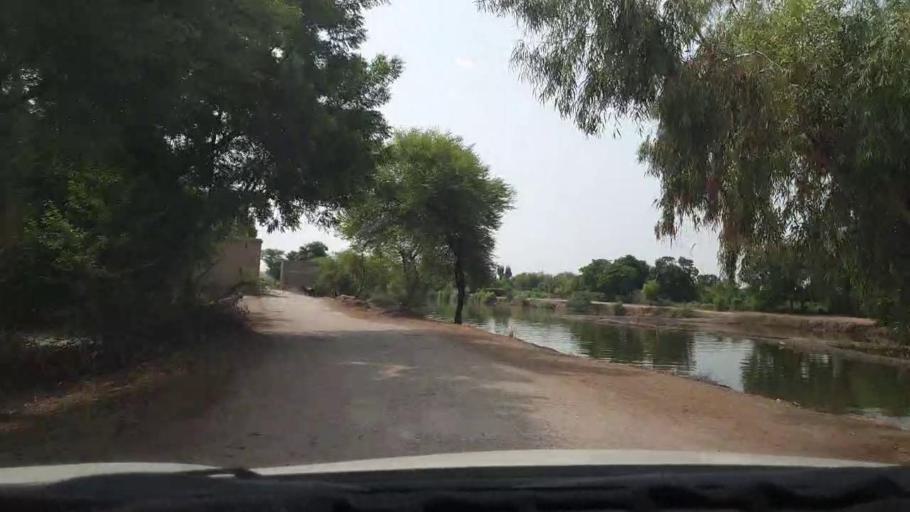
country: PK
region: Sindh
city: Dokri
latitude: 27.3875
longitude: 68.1224
